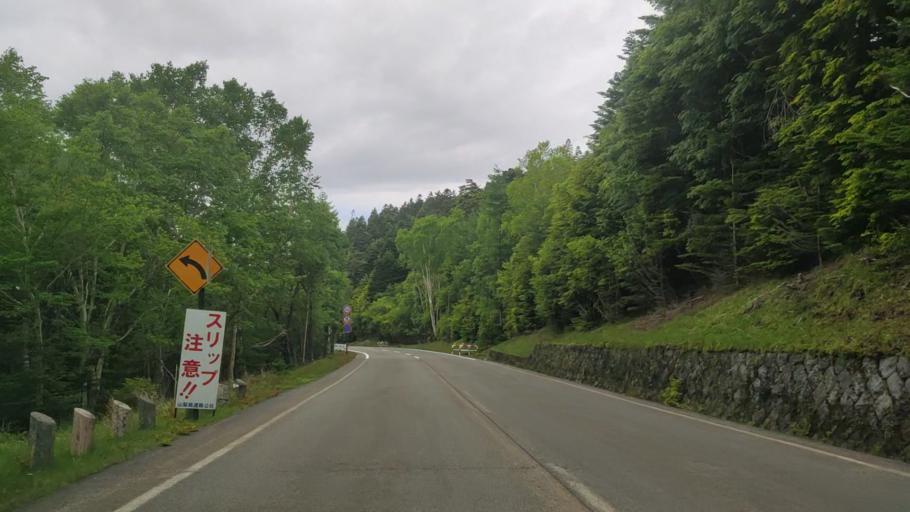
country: JP
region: Yamanashi
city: Fujikawaguchiko
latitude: 35.3823
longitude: 138.6908
